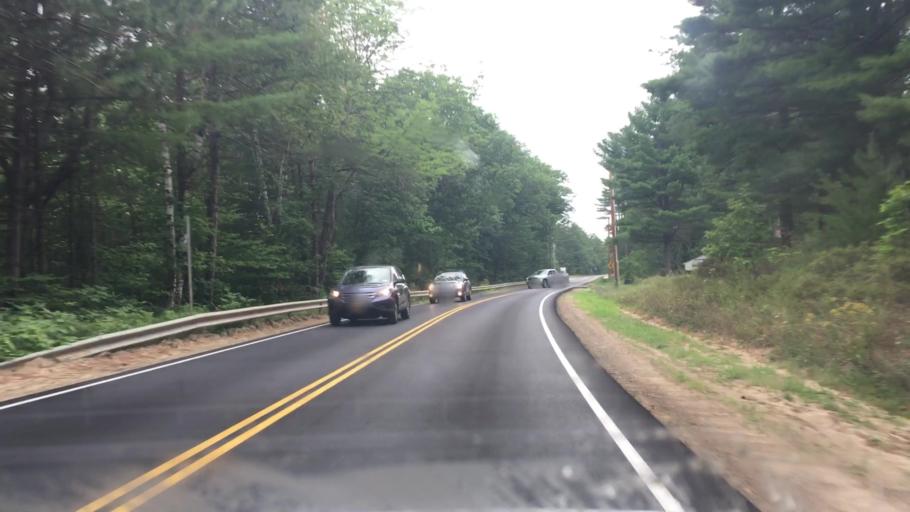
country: US
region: New York
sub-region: Clinton County
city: Morrisonville
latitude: 44.6222
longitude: -73.6054
